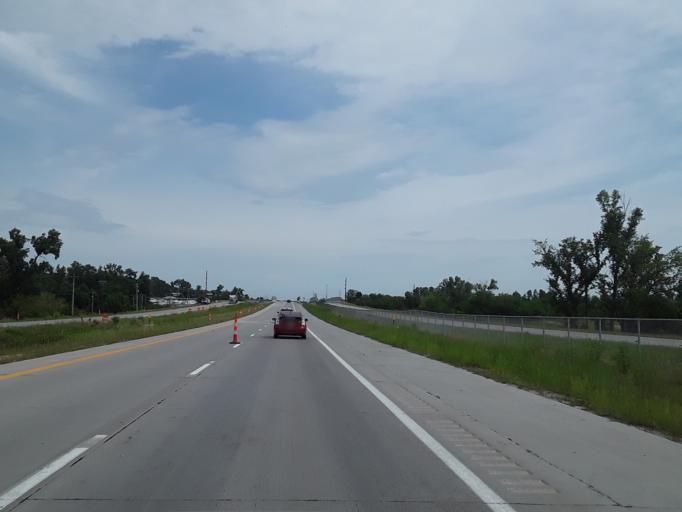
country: US
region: Nebraska
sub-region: Sarpy County
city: Offutt Air Force Base
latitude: 41.0655
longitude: -95.9278
